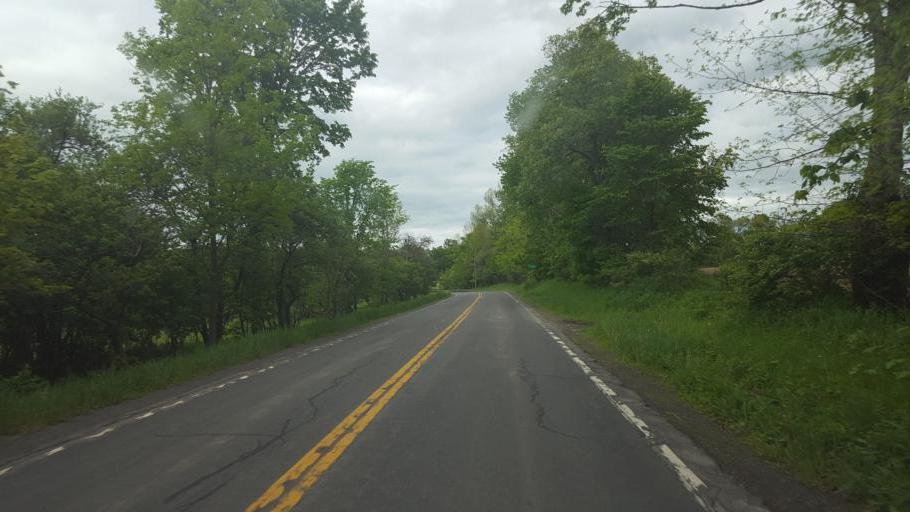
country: US
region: New York
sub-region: Otsego County
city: Richfield Springs
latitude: 42.8791
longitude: -74.9658
